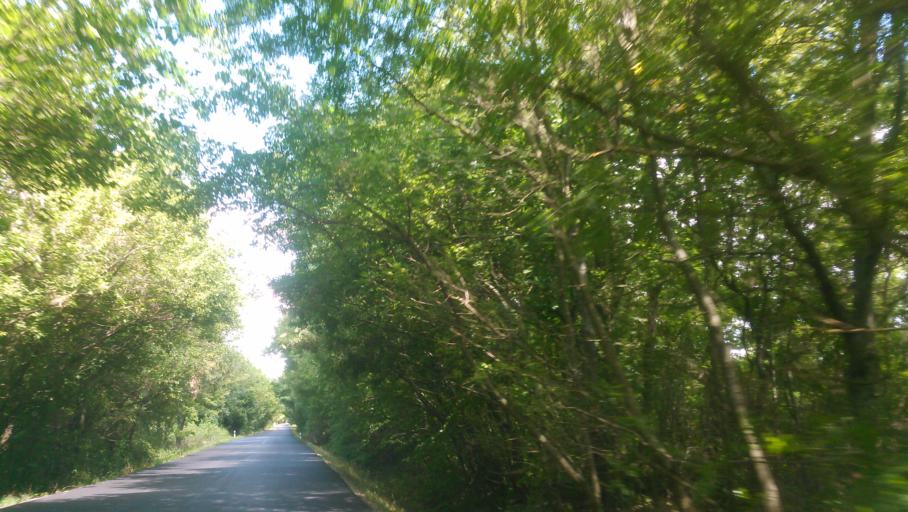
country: SK
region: Trnavsky
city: Leopoldov
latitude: 48.5067
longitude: 17.7361
